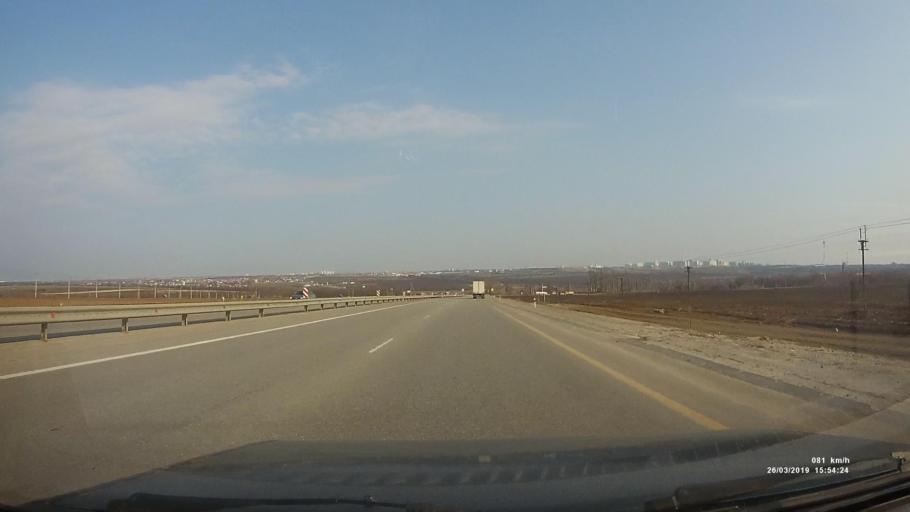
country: RU
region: Rostov
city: Krym
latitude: 47.2698
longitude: 39.5575
